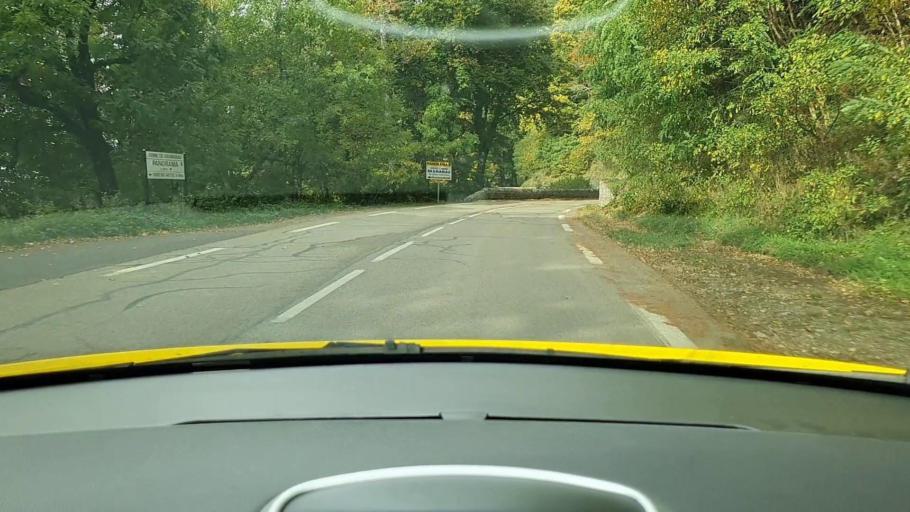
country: FR
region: Languedoc-Roussillon
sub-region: Departement de la Lozere
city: Meyrueis
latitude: 44.1236
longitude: 3.4773
